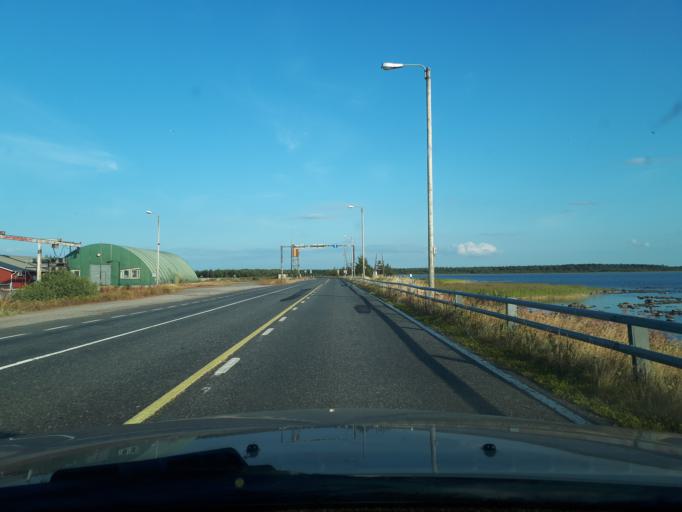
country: FI
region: Northern Ostrobothnia
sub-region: Oulu
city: Lumijoki
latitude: 65.0071
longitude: 25.2011
